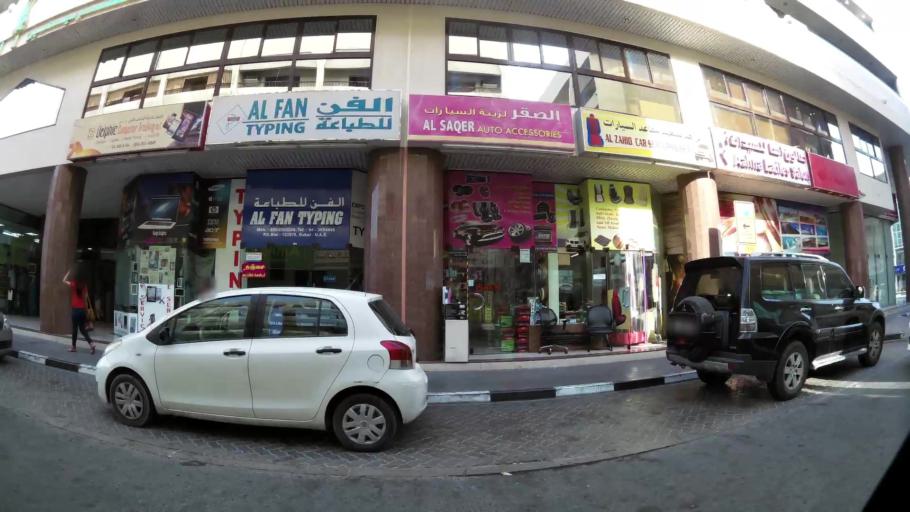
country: AE
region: Ash Shariqah
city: Sharjah
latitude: 25.2451
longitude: 55.3066
